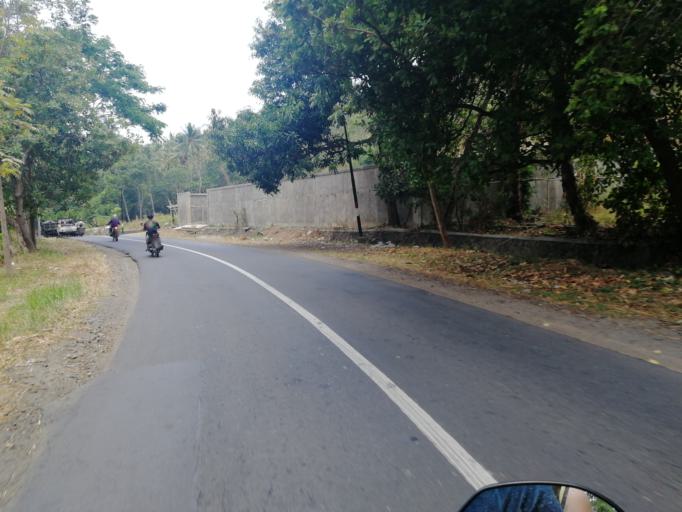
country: ID
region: West Nusa Tenggara
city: Karangsubagan
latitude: -8.4138
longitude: 116.0991
